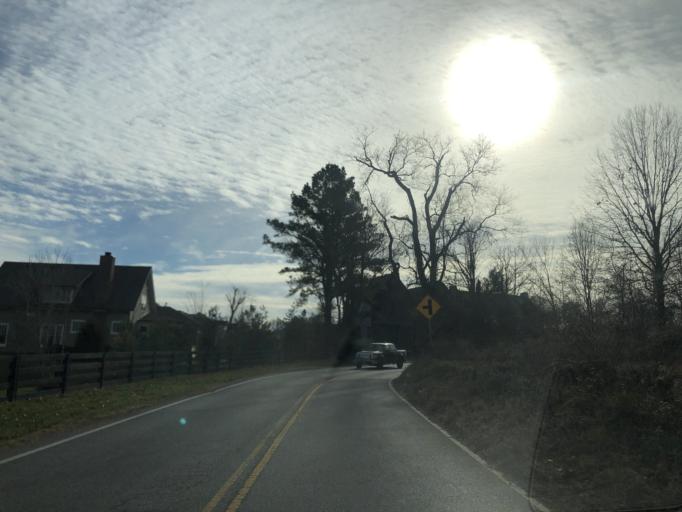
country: US
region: Tennessee
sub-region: Williamson County
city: Franklin
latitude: 35.9381
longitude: -86.9033
